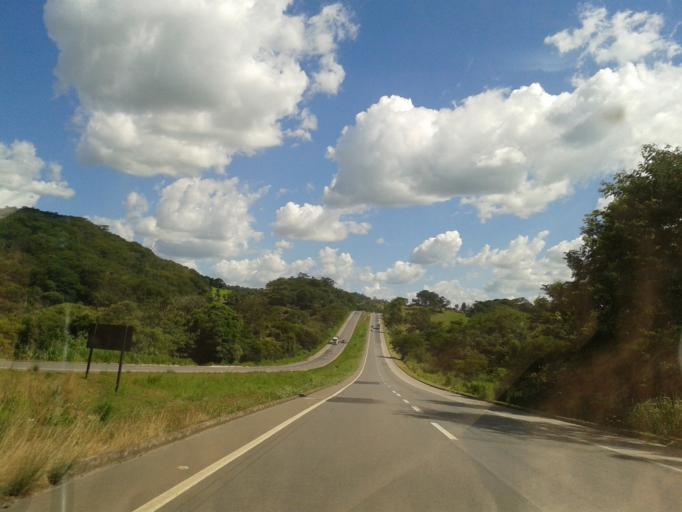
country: BR
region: Goias
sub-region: Morrinhos
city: Morrinhos
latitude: -17.5912
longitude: -49.1926
